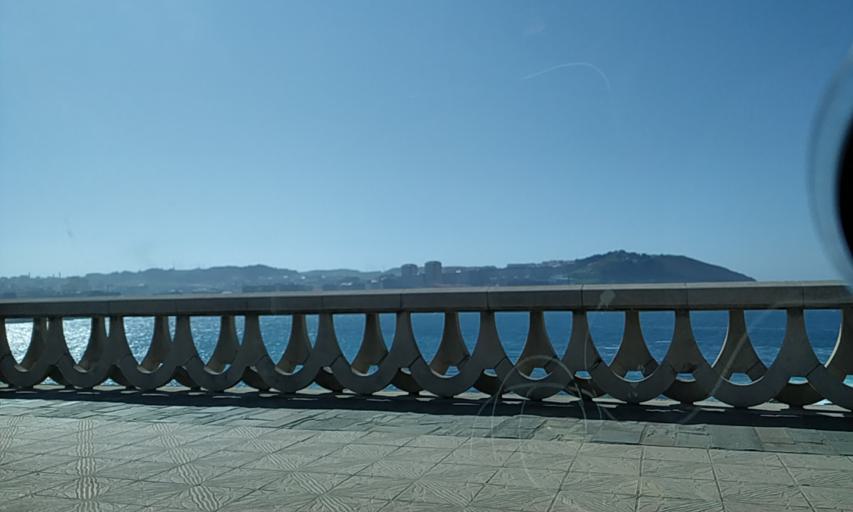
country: ES
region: Galicia
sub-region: Provincia da Coruna
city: A Coruna
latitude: 43.3785
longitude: -8.4077
